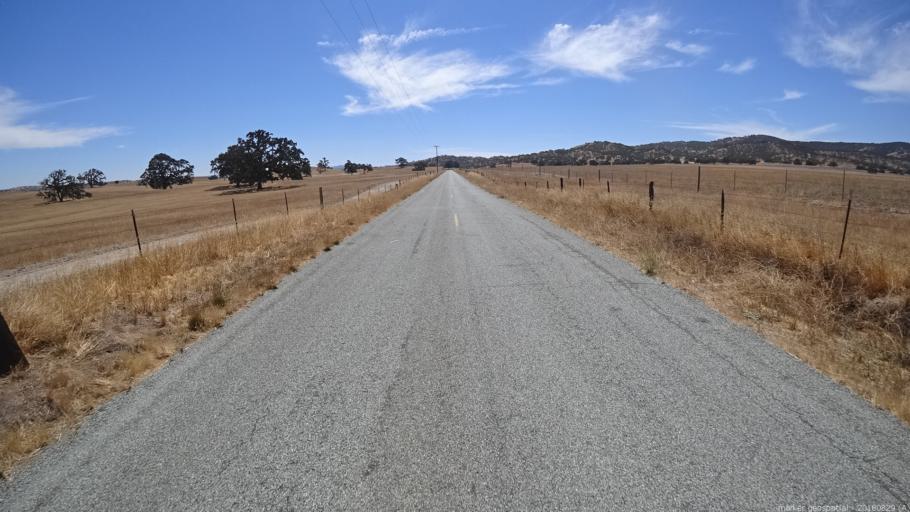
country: US
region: California
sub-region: San Luis Obispo County
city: Lake Nacimiento
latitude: 35.8404
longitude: -120.8432
